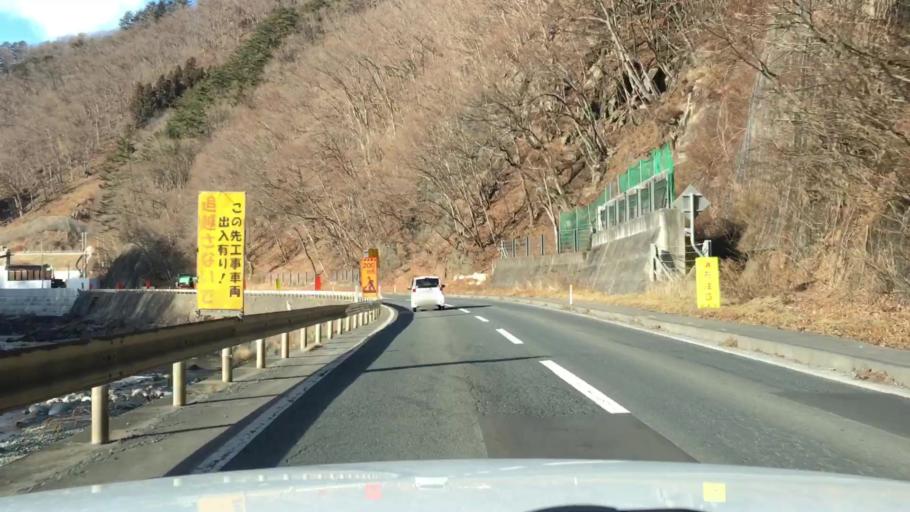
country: JP
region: Iwate
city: Miyako
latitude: 39.5999
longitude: 141.7131
